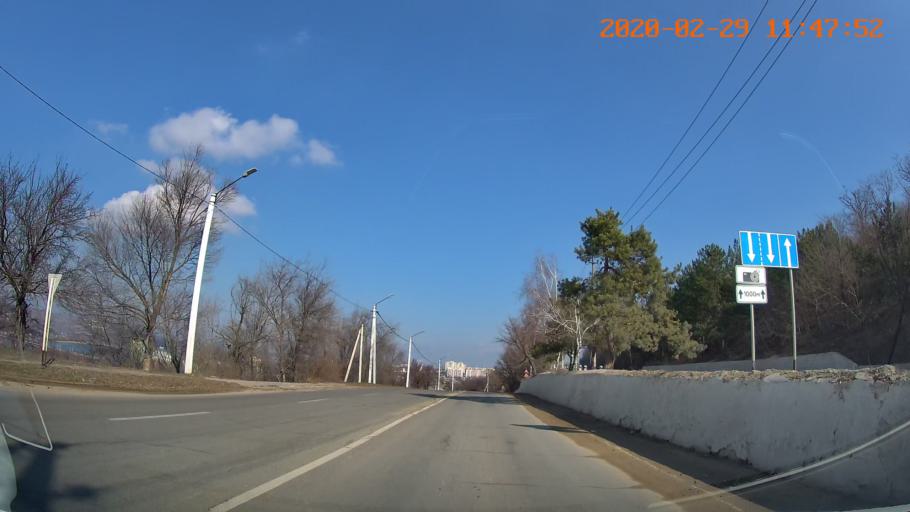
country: MD
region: Rezina
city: Rezina
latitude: 47.7443
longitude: 28.9877
